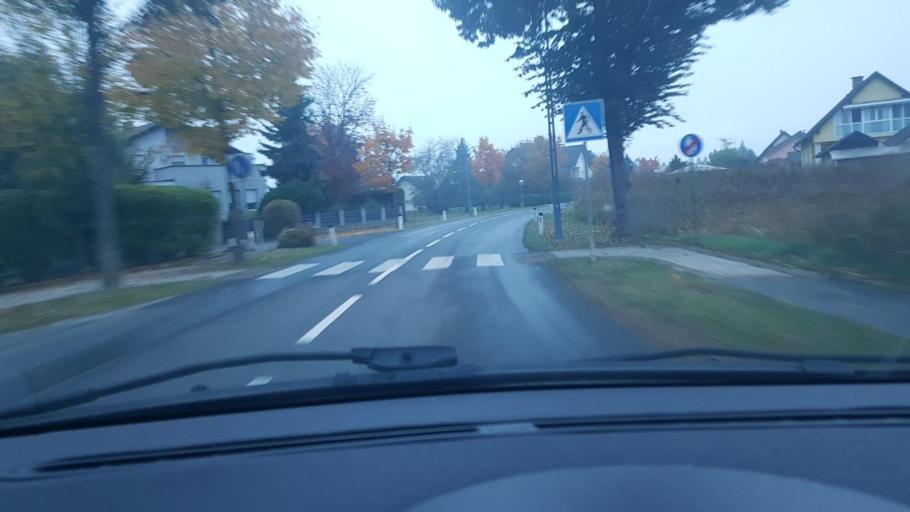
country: AT
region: Styria
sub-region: Politischer Bezirk Leibnitz
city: Obervogau
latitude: 46.7392
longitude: 15.5816
